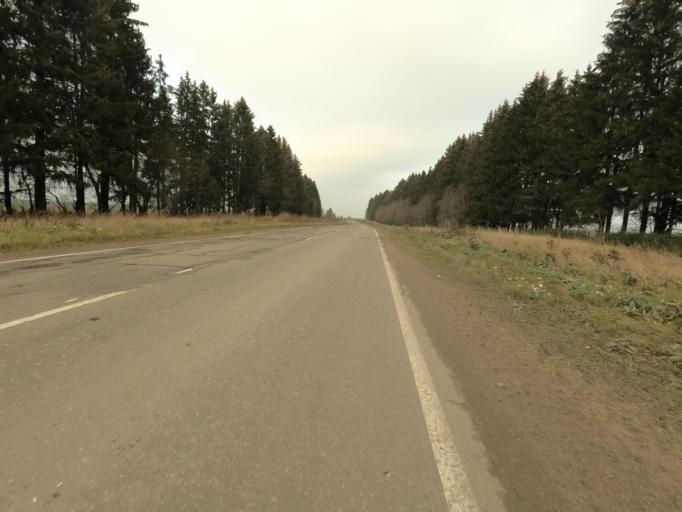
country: RU
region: Leningrad
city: Mga
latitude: 59.7787
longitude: 31.0246
